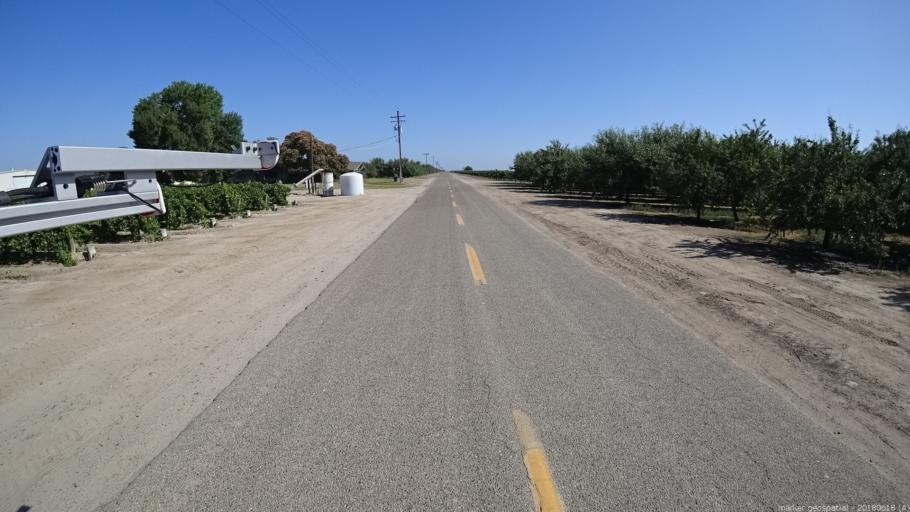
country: US
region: California
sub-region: Madera County
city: Parkwood
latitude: 36.8434
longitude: -120.1465
